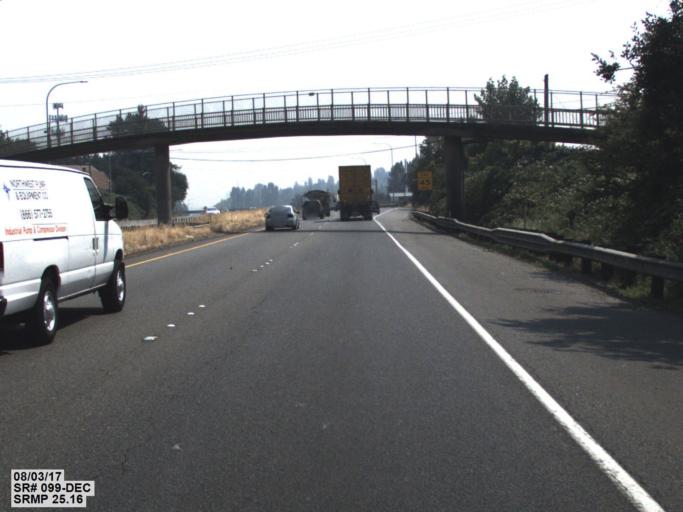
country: US
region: Washington
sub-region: King County
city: White Center
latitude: 47.5235
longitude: -122.3217
